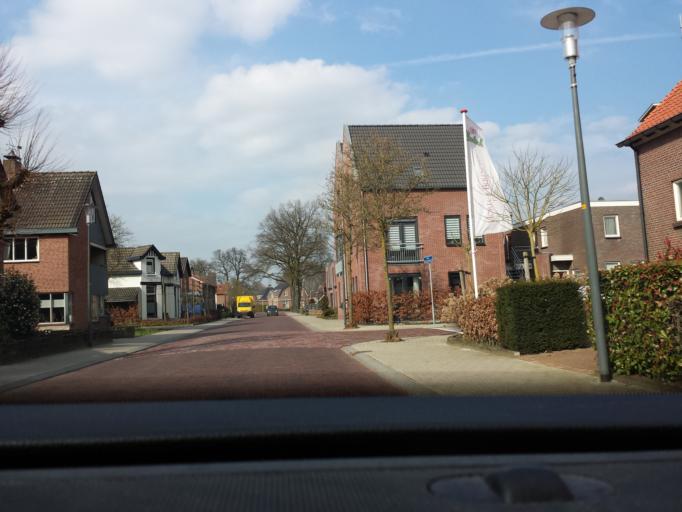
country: NL
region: Gelderland
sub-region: Oost Gelre
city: Lichtenvoorde
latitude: 52.0049
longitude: 6.5195
